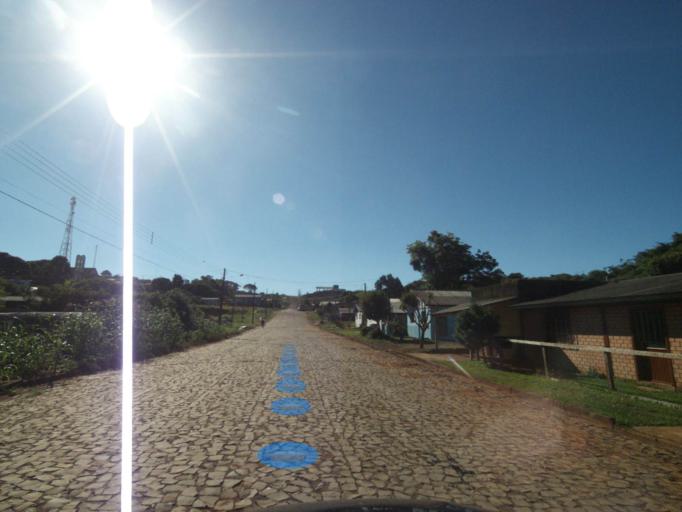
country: BR
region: Parana
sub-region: Coronel Vivida
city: Coronel Vivida
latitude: -26.1415
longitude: -52.3861
